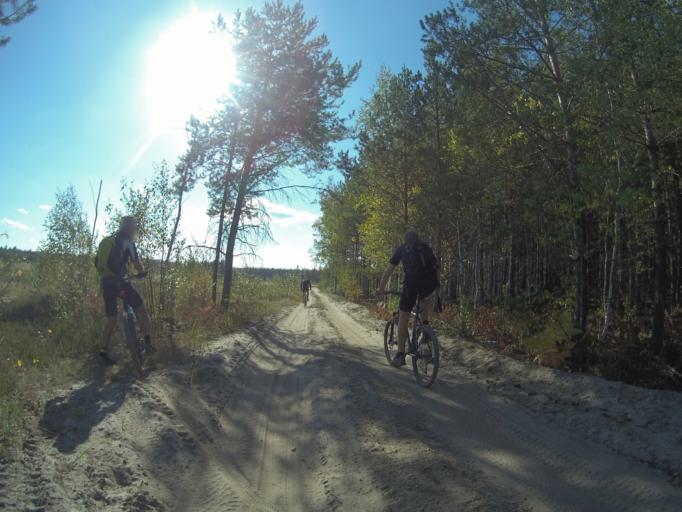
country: RU
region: Vladimir
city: Vorsha
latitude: 55.8899
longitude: 40.1795
